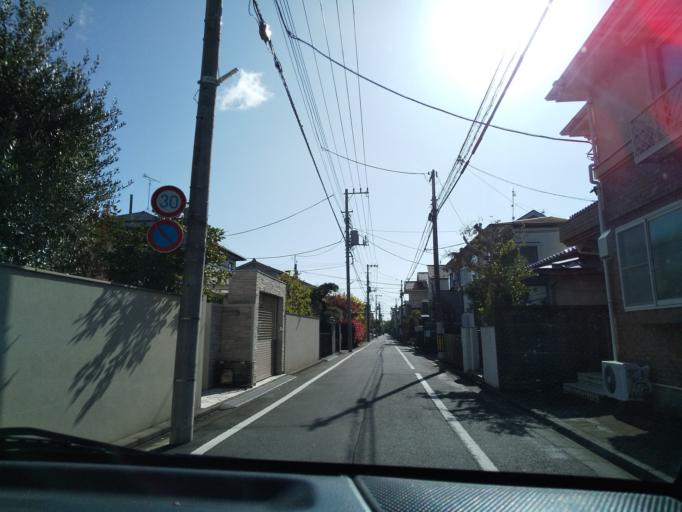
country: JP
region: Tokyo
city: Hino
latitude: 35.6919
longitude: 139.4353
